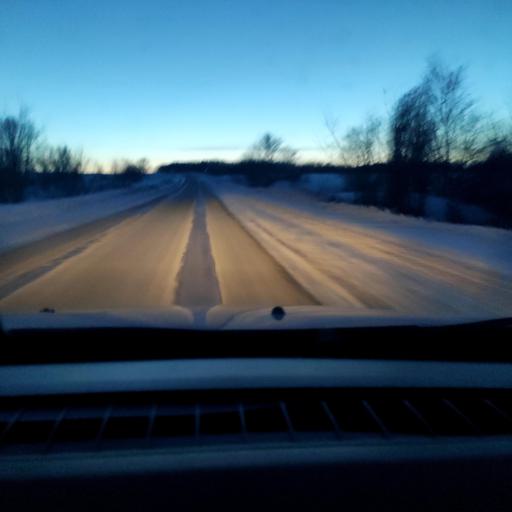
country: RU
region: Samara
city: Georgiyevka
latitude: 53.3152
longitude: 50.8498
